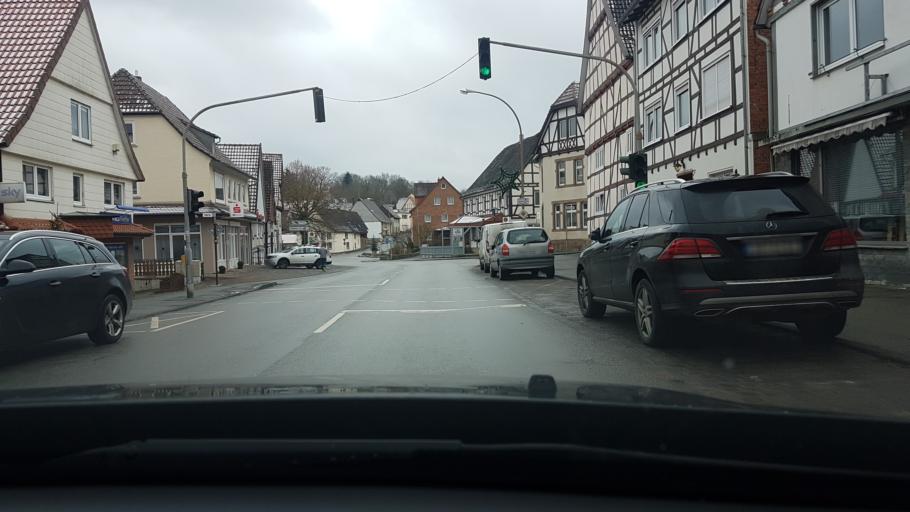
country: DE
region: Hesse
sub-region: Regierungsbezirk Kassel
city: Bad Arolsen
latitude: 51.4734
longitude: 9.0111
